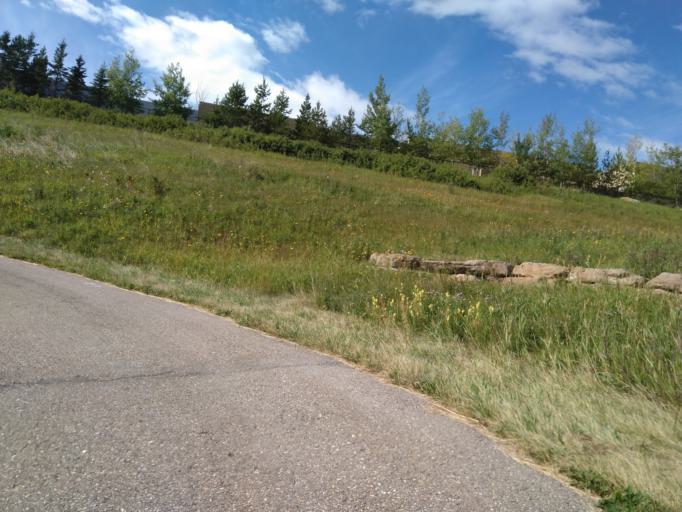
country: CA
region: Alberta
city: Calgary
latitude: 51.1591
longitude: -114.1577
